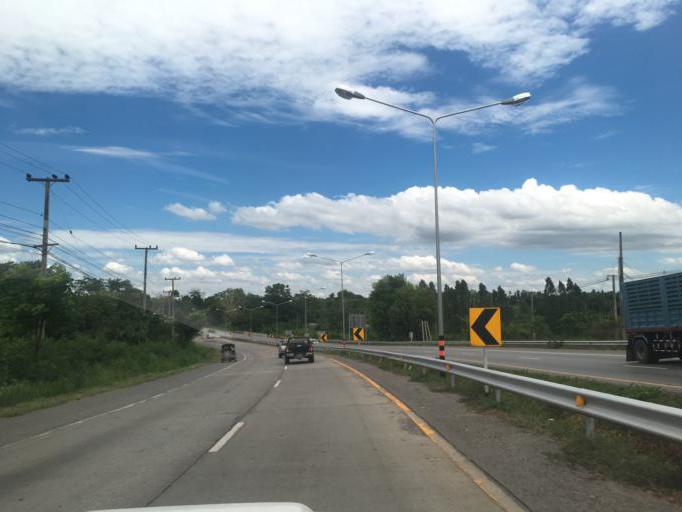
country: TH
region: Khon Kaen
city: Nam Phong
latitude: 16.6283
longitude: 102.7994
